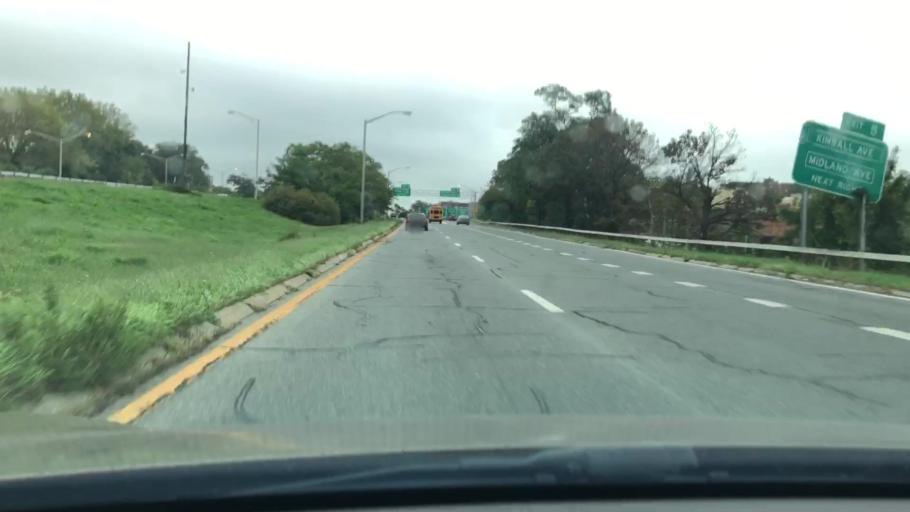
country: US
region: New York
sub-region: Westchester County
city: Bronxville
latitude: 40.9301
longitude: -73.8527
